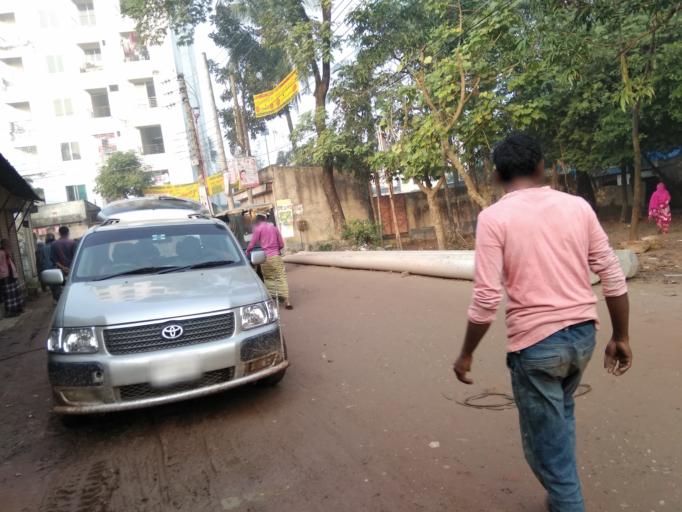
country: BD
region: Dhaka
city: Tungi
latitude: 23.8617
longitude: 90.4329
